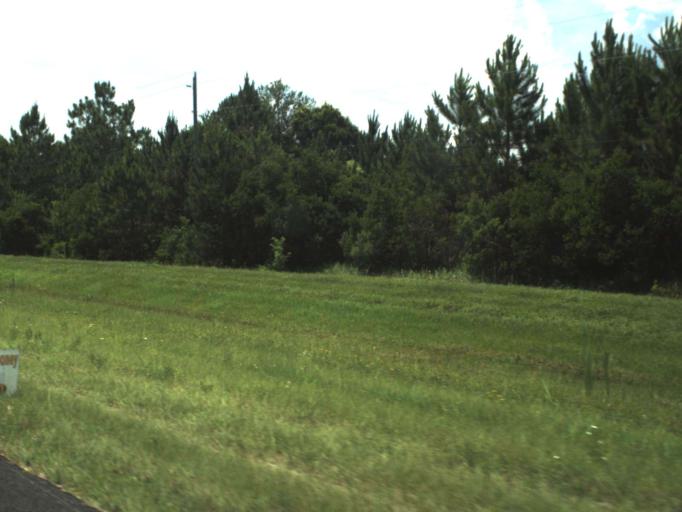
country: US
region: Florida
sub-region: Volusia County
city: Samsula-Spruce Creek
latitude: 29.0114
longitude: -81.0641
